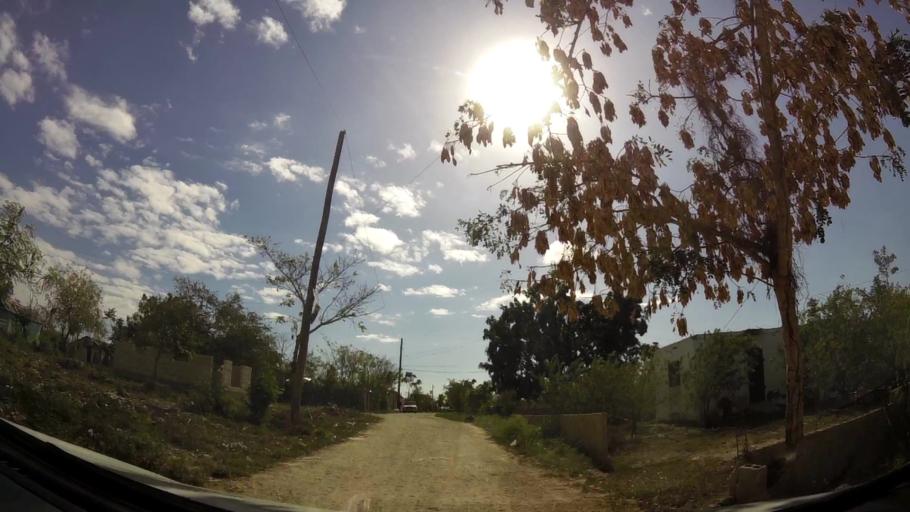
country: DO
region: Santo Domingo
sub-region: Santo Domingo
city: Boca Chica
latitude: 18.4644
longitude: -69.6038
